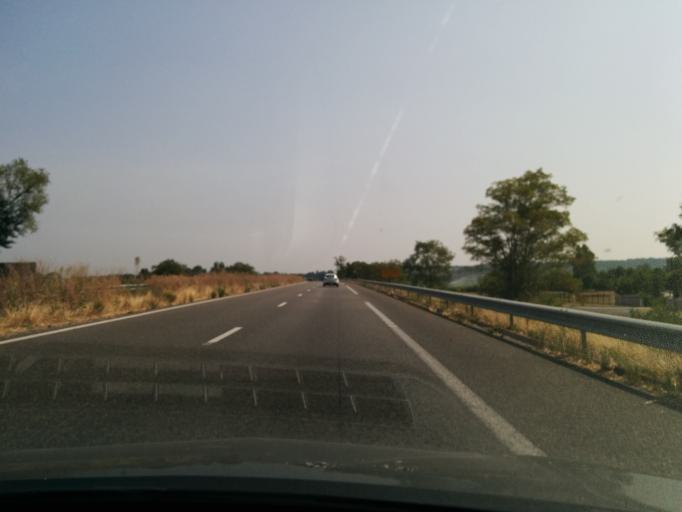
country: FR
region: Midi-Pyrenees
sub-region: Departement du Tarn
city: Saint-Sulpice-la-Pointe
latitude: 43.7639
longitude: 1.7179
